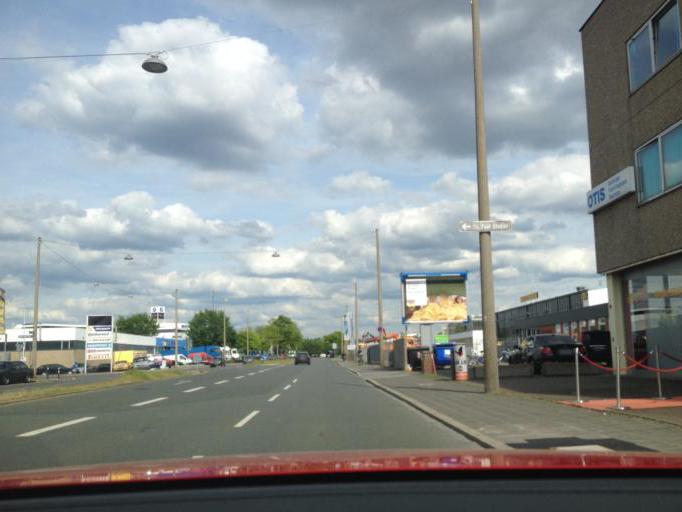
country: DE
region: Bavaria
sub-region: Regierungsbezirk Mittelfranken
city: Wetzendorf
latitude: 49.4472
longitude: 11.0430
